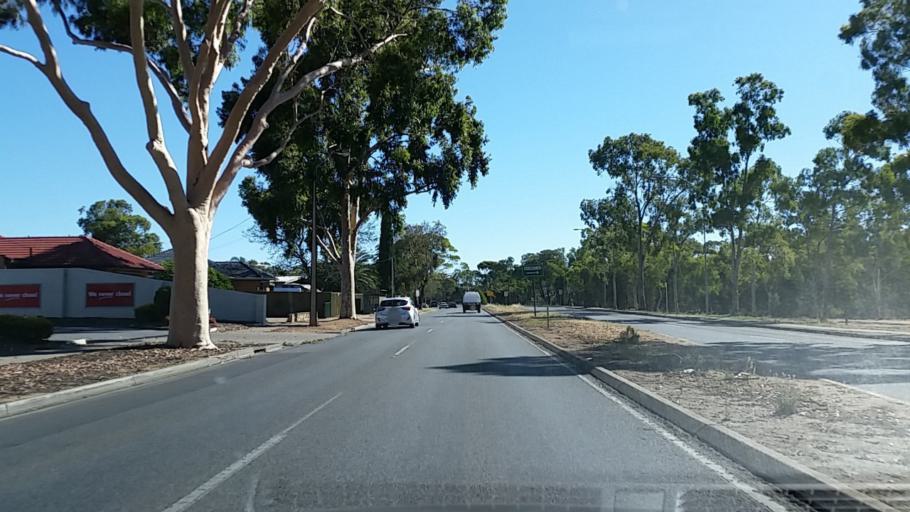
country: AU
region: South Australia
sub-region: Salisbury
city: Ingle Farm
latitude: -34.8137
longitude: 138.6431
